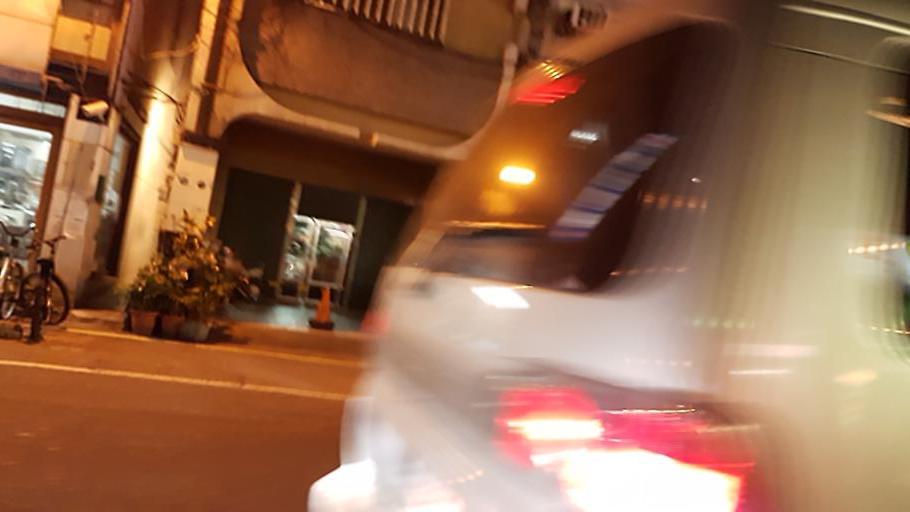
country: TW
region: Taiwan
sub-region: Changhua
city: Chang-hua
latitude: 24.0781
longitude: 120.5390
